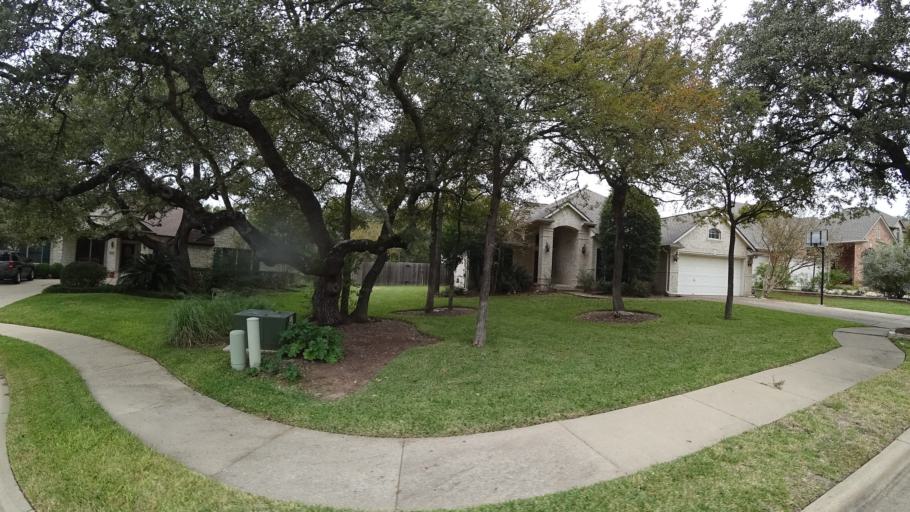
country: US
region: Texas
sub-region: Williamson County
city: Anderson Mill
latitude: 30.4485
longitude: -97.8221
